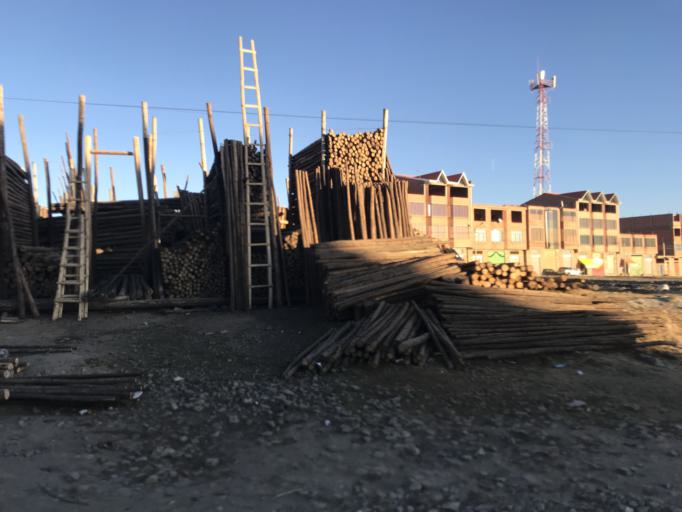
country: BO
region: La Paz
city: La Paz
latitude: -16.4999
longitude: -68.2351
